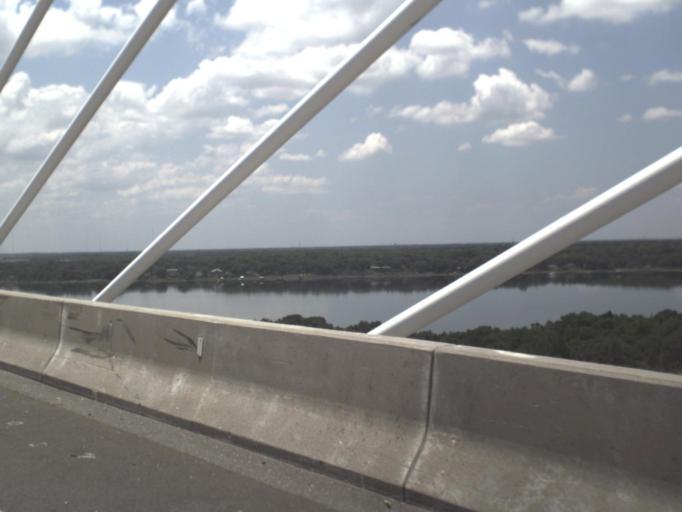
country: US
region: Florida
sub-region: Duval County
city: Jacksonville
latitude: 30.3851
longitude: -81.5573
